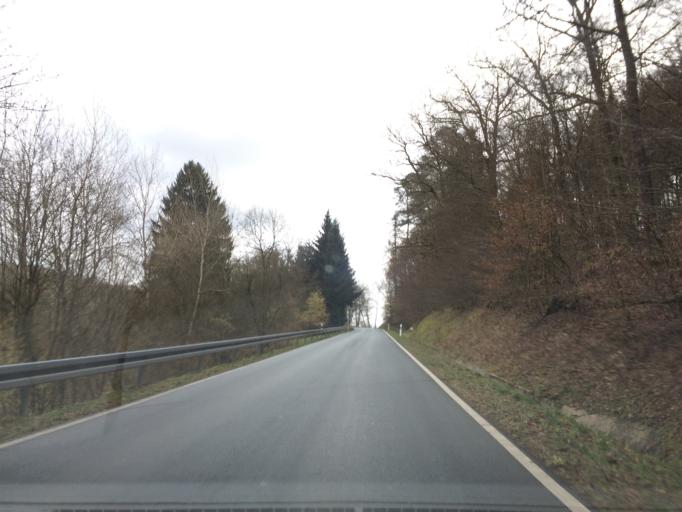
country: DE
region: Hesse
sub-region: Regierungsbezirk Darmstadt
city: Gravenwiesbach
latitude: 50.3791
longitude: 8.4384
